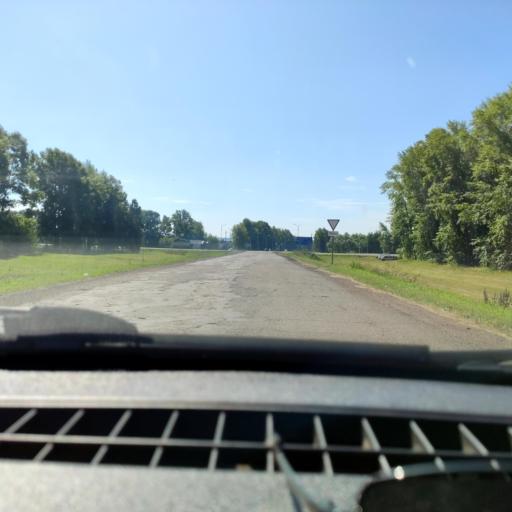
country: RU
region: Bashkortostan
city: Karmaskaly
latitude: 54.3872
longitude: 56.1771
